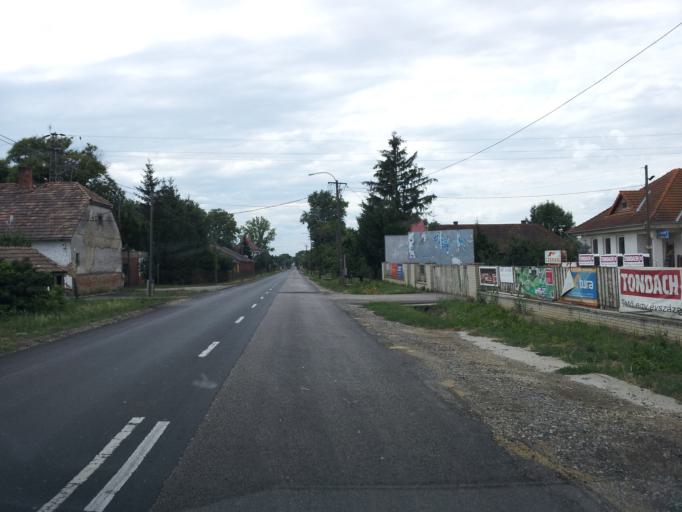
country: HU
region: Fejer
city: Enying
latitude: 46.9201
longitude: 18.2640
